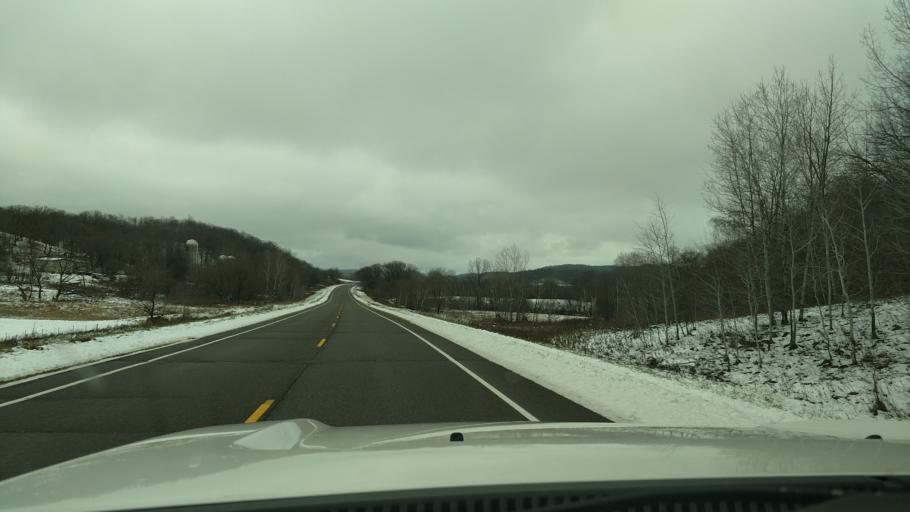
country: US
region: Wisconsin
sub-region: Dunn County
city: Tainter Lake
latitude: 45.1357
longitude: -91.8049
